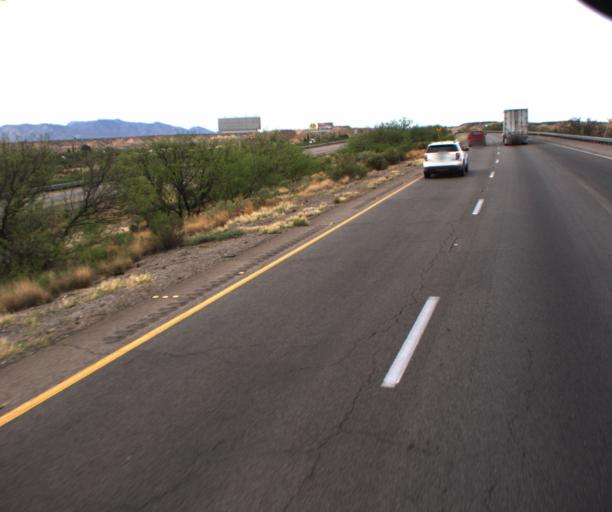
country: US
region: Arizona
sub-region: Cochise County
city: Benson
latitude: 31.9779
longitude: -110.3126
